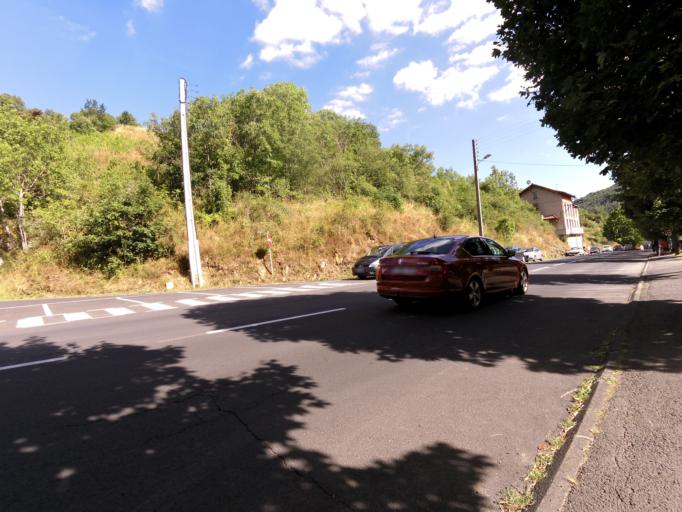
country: FR
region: Auvergne
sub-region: Departement du Puy-de-Dome
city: Aydat
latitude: 45.5860
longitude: 2.9917
